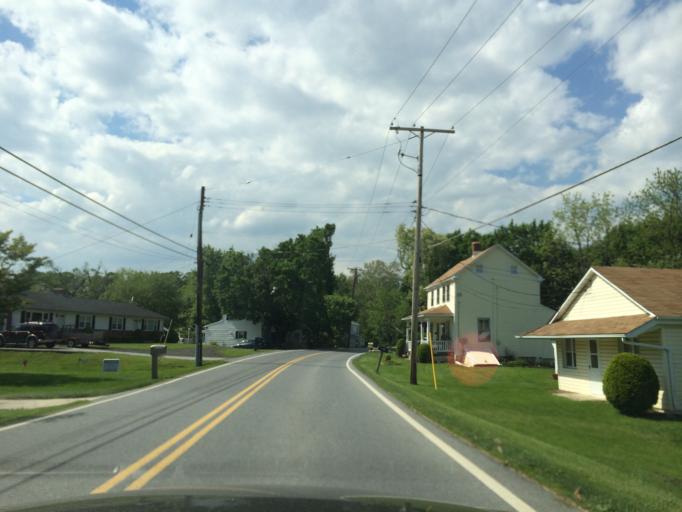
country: US
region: Maryland
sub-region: Carroll County
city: Sykesville
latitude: 39.4339
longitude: -77.0536
